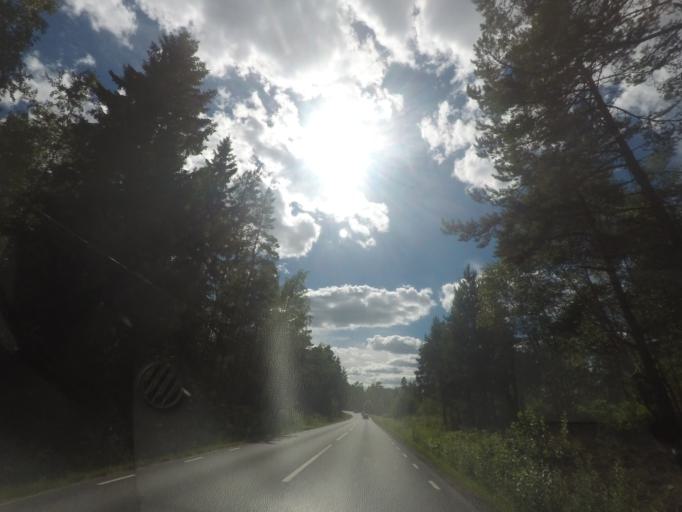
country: SE
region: Stockholm
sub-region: Norrtalje Kommun
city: Arno
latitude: 60.0875
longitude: 18.7889
